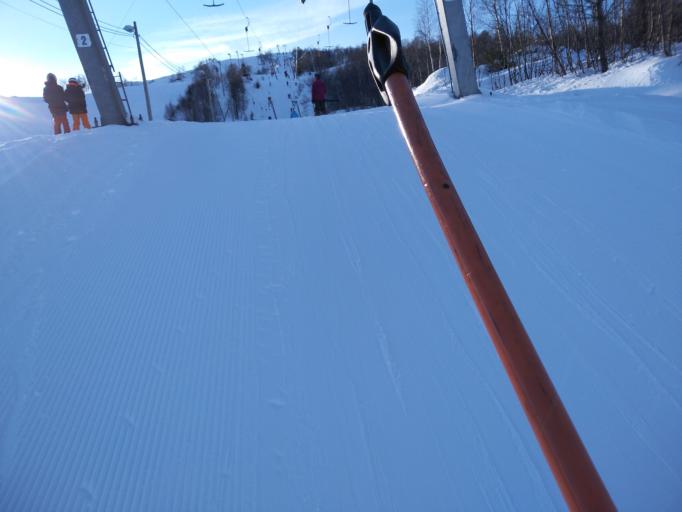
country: NO
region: Rogaland
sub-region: Sauda
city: Sauda
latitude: 59.6230
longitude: 6.2415
